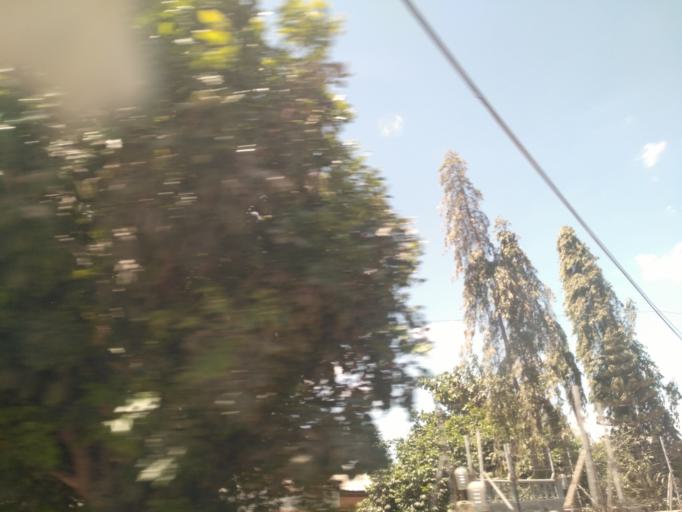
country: TZ
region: Dodoma
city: Dodoma
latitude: -6.1699
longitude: 35.7402
